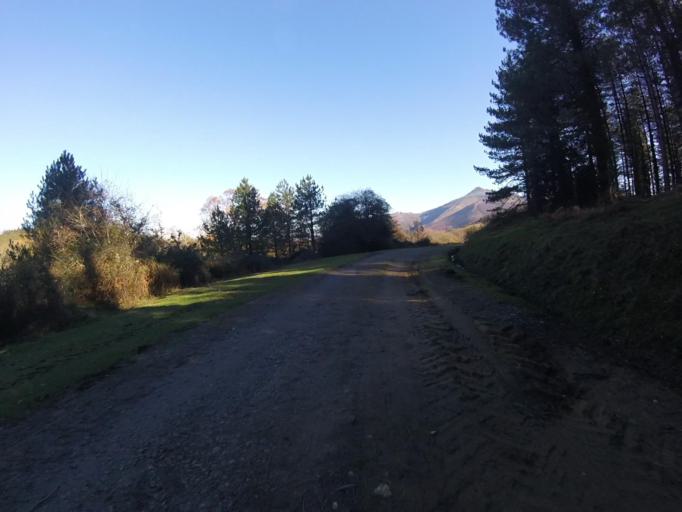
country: ES
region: Navarre
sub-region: Provincia de Navarra
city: Bera
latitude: 43.3186
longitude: -1.6927
